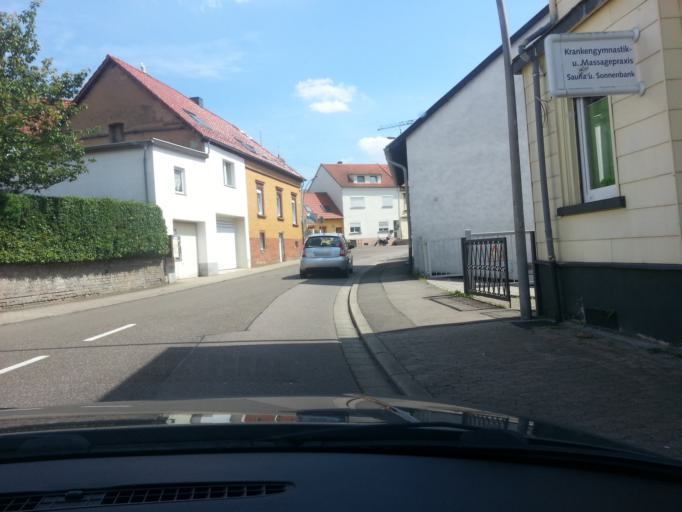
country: DE
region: Saarland
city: Spiesen-Elversberg
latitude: 49.2852
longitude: 7.1621
